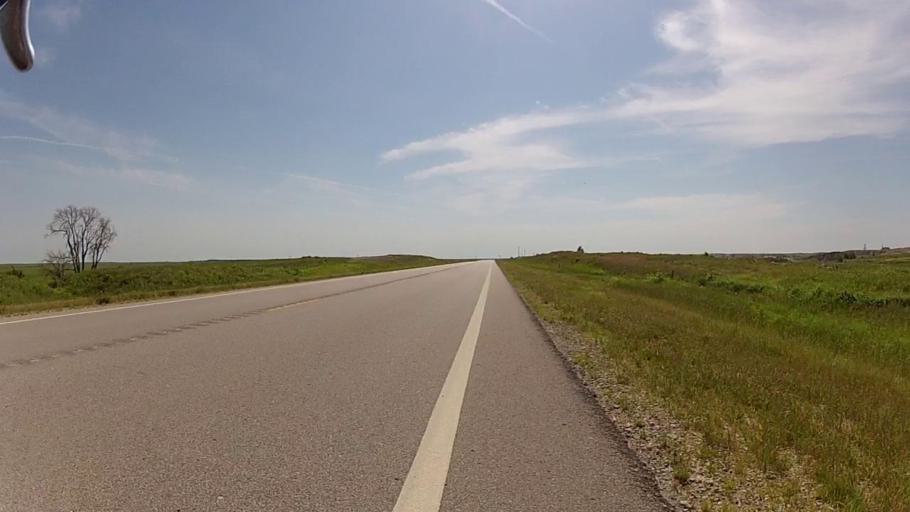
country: US
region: Kansas
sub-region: Cowley County
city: Winfield
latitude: 37.1110
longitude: -96.6119
